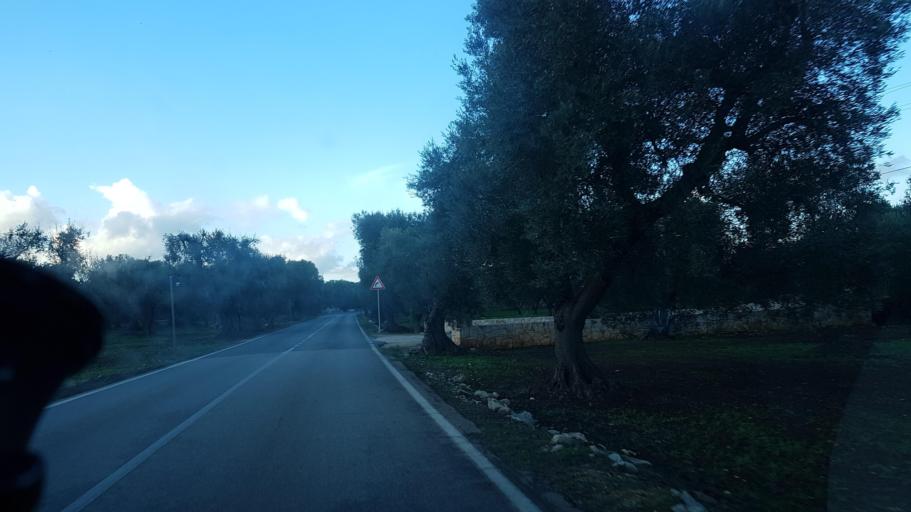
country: IT
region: Apulia
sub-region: Provincia di Brindisi
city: San Michele Salentino
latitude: 40.6552
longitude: 17.6035
